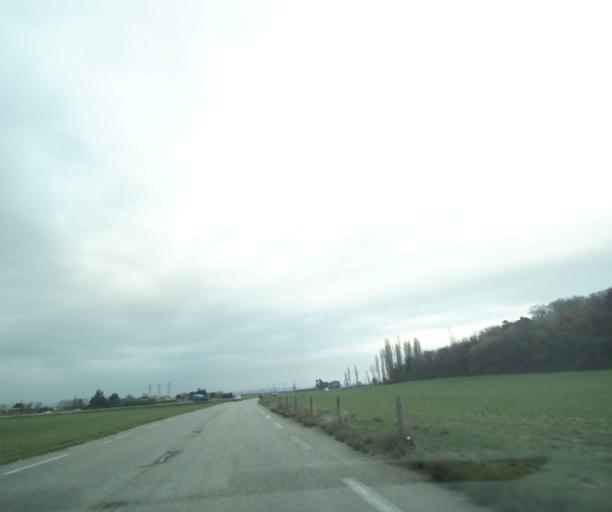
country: FR
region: Rhone-Alpes
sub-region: Departement de la Drome
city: Bourg-les-Valence
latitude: 44.9805
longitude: 4.9013
